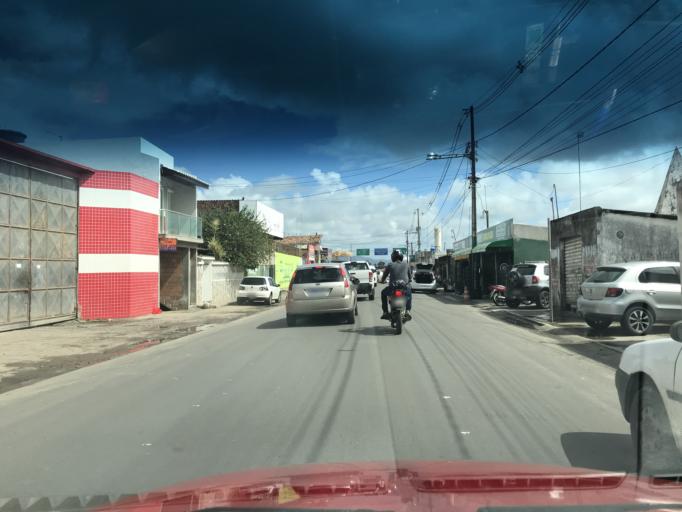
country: BR
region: Bahia
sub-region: Santo Antonio De Jesus
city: Santo Antonio de Jesus
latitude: -12.9649
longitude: -39.2702
